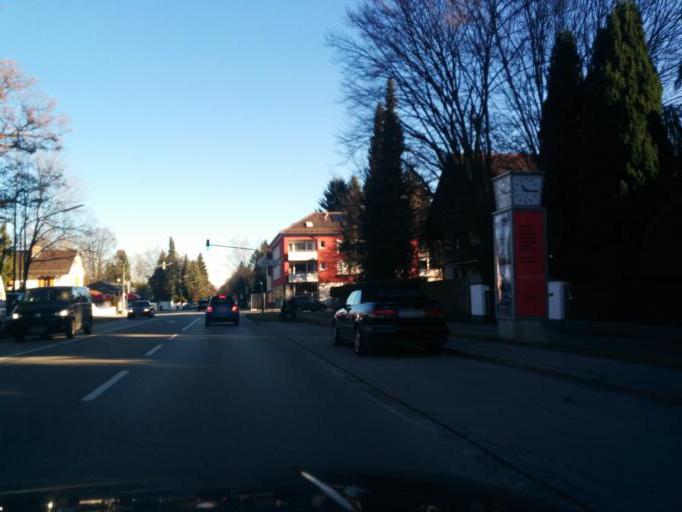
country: DE
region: Bavaria
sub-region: Upper Bavaria
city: Grunwald
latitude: 48.0499
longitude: 11.5333
